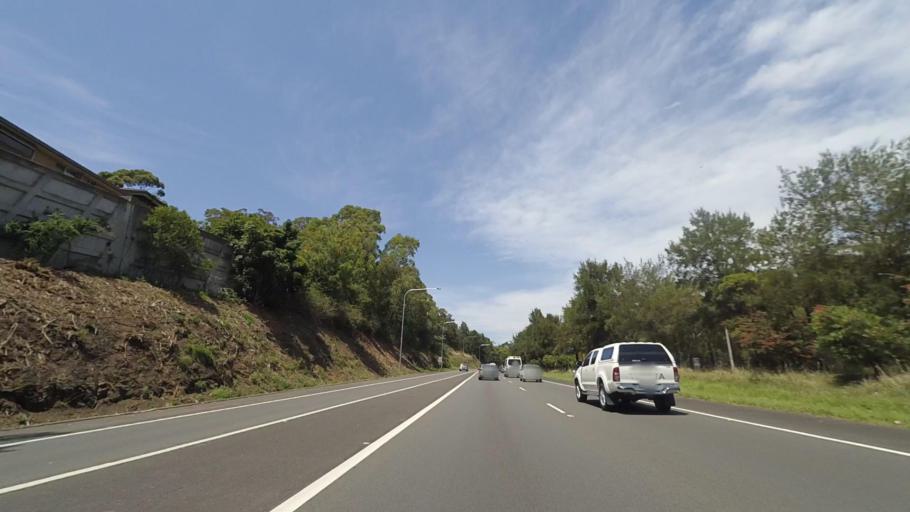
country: AU
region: New South Wales
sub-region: Wollongong
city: Mangerton
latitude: -34.4312
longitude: 150.8679
